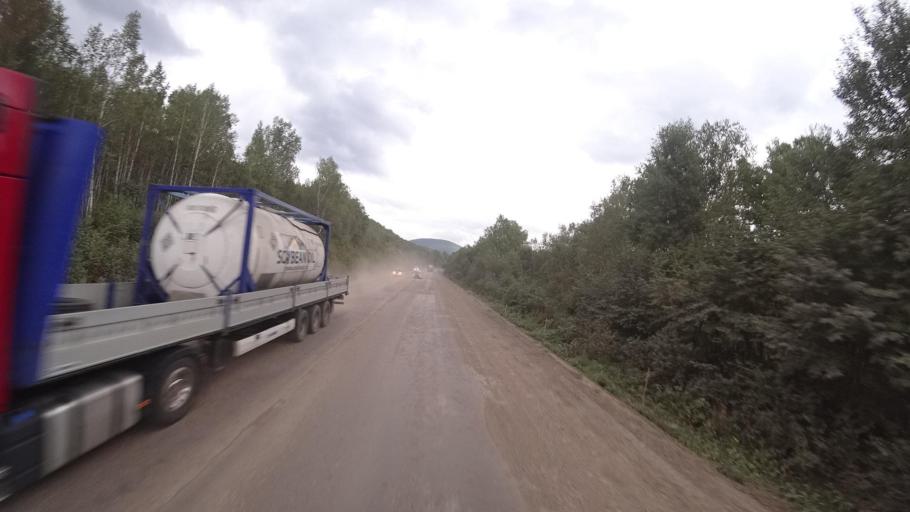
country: RU
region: Jewish Autonomous Oblast
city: Khingansk
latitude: 48.9915
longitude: 131.1090
